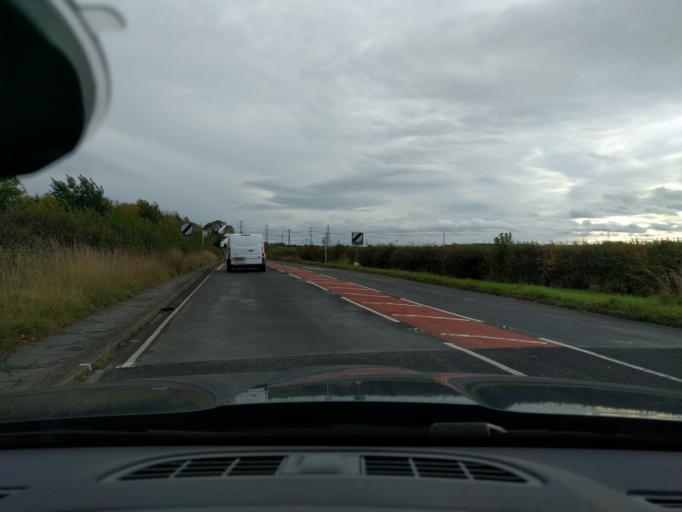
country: GB
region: England
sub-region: Northumberland
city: Bedlington
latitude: 55.1224
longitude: -1.5777
